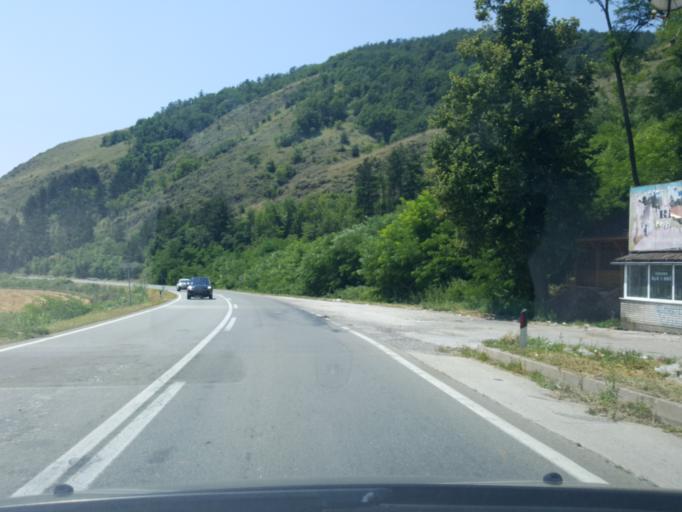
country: RS
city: Prislonica
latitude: 43.9948
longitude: 20.4225
